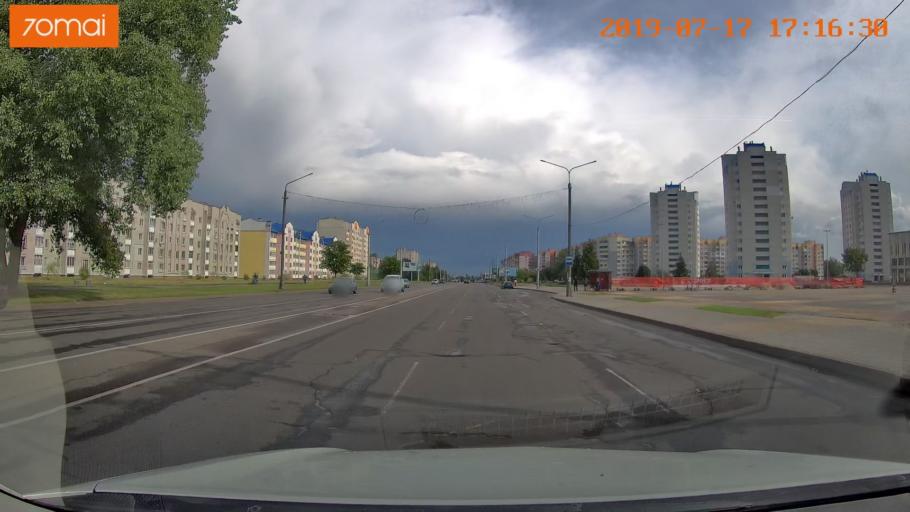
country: BY
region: Mogilev
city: Babruysk
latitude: 53.1676
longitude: 29.1934
